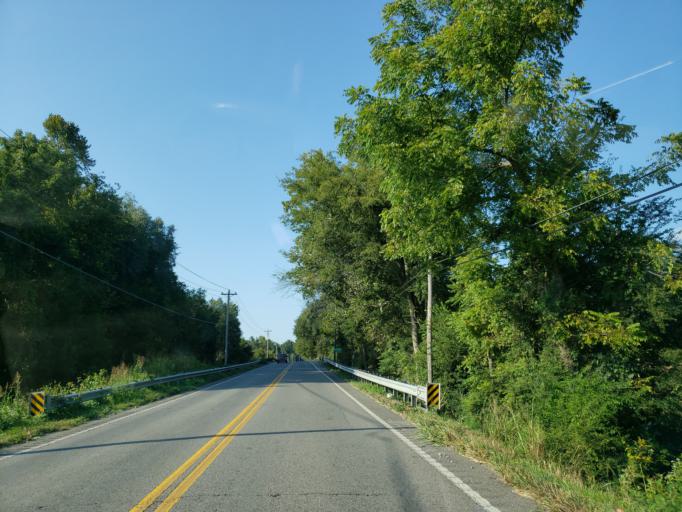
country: US
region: Tennessee
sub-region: Bradley County
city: Wildwood Lake
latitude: 35.0085
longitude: -84.7340
